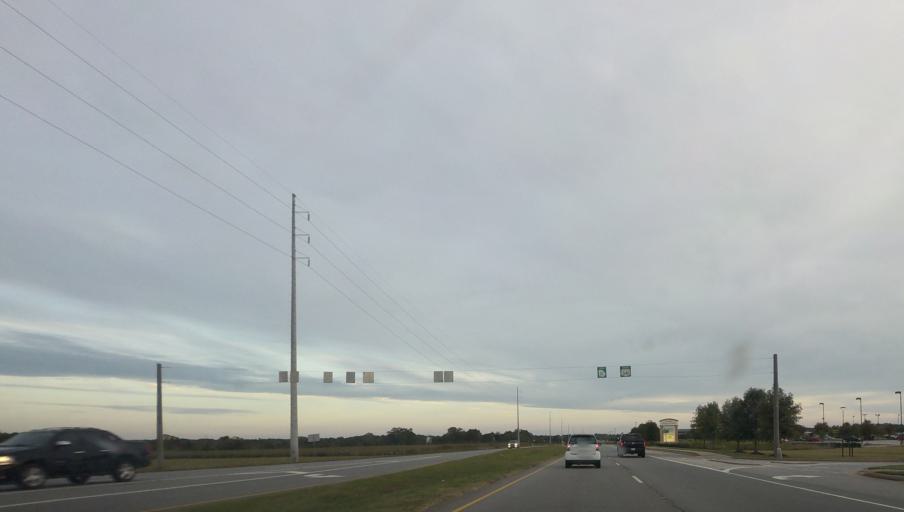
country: US
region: Georgia
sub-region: Houston County
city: Perry
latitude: 32.4749
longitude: -83.7054
